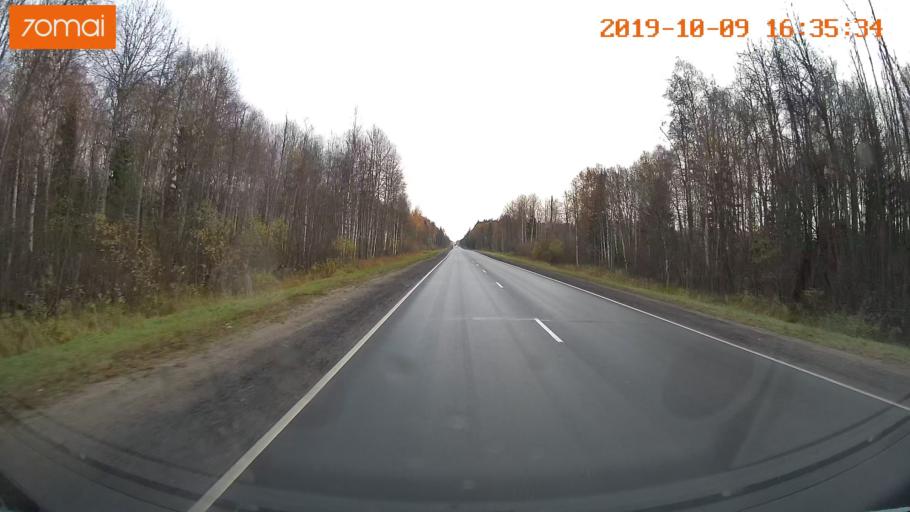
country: RU
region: Kostroma
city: Oktyabr'skiy
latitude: 57.5537
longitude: 41.0026
